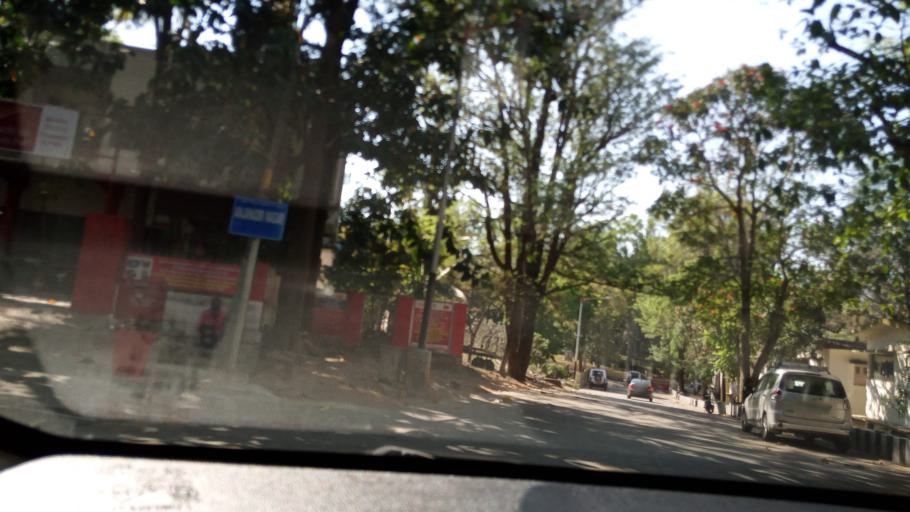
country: IN
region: Andhra Pradesh
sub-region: Chittoor
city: Tirumala
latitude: 13.6777
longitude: 79.3492
